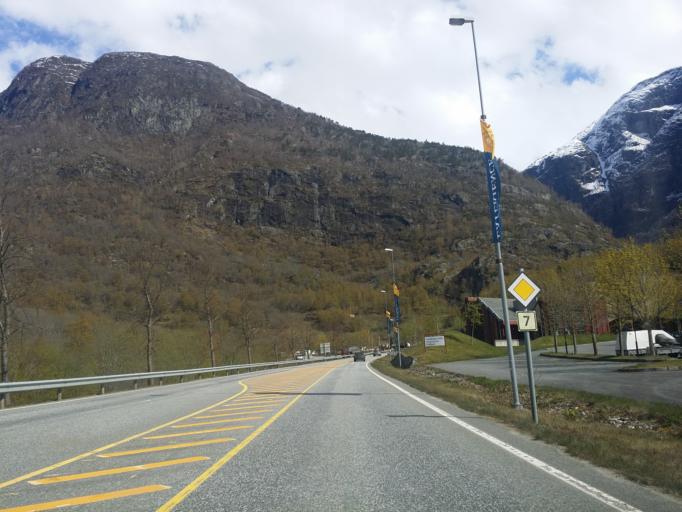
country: NO
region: Hordaland
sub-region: Eidfjord
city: Eidfjord
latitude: 60.4238
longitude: 7.1325
